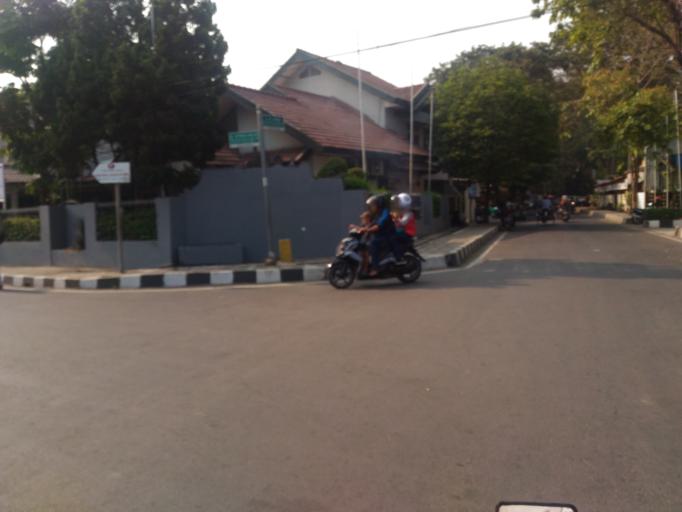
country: ID
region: Banten
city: Tangerang
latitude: -6.1722
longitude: 106.6329
